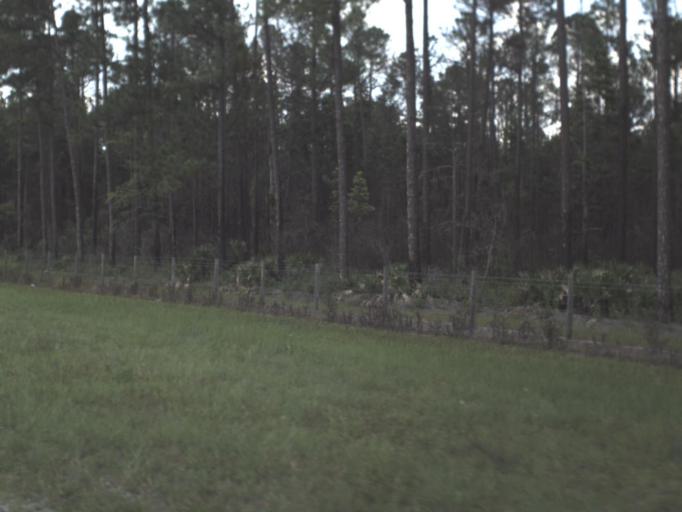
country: US
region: Florida
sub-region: Bradford County
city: Starke
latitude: 29.9953
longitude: -82.0277
